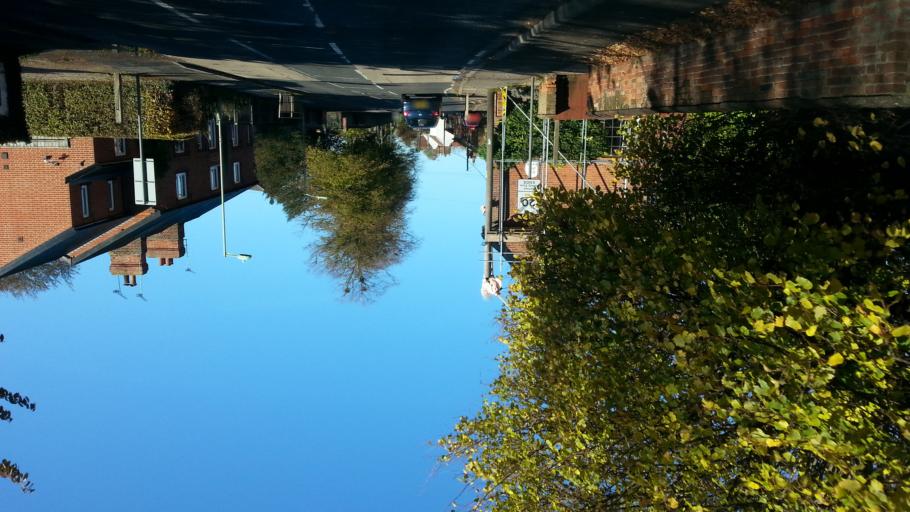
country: GB
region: England
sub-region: Suffolk
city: Wickham Market
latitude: 52.1153
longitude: 1.3819
